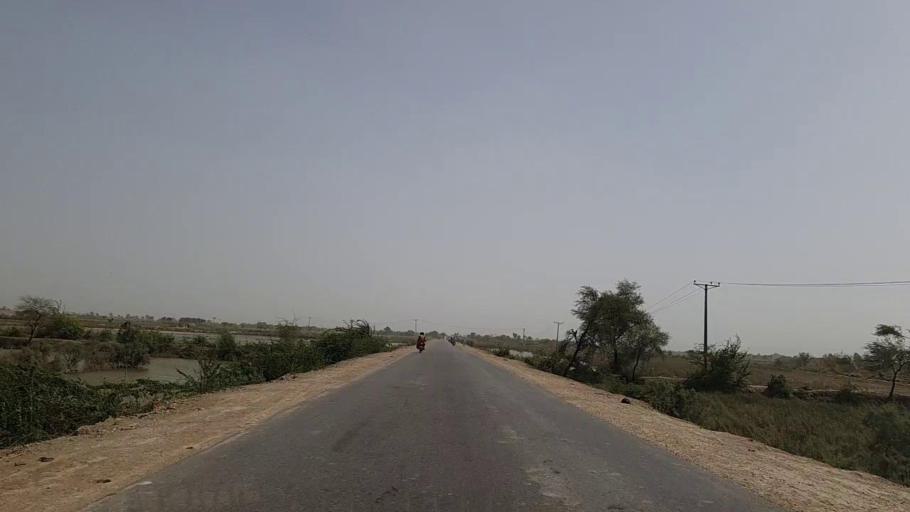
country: PK
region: Sindh
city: Talhar
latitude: 24.8661
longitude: 68.8450
